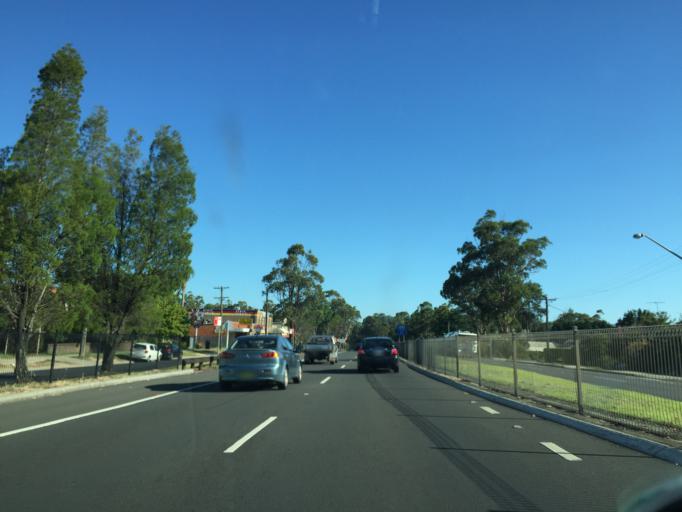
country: AU
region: New South Wales
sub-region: Blue Mountains Municipality
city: Glenbrook
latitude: -33.7562
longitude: 150.6119
